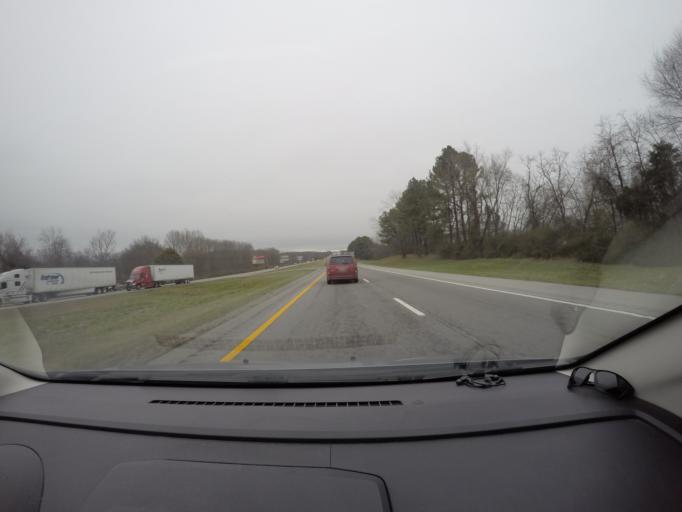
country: US
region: Tennessee
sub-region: Franklin County
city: Sewanee
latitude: 35.3627
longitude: -85.9614
